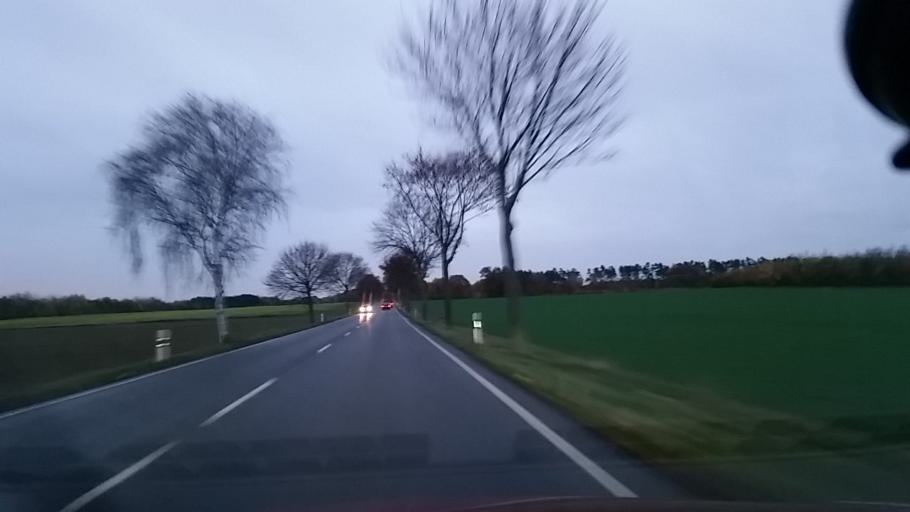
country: DE
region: Lower Saxony
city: Wrestedt
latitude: 52.9380
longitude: 10.5955
